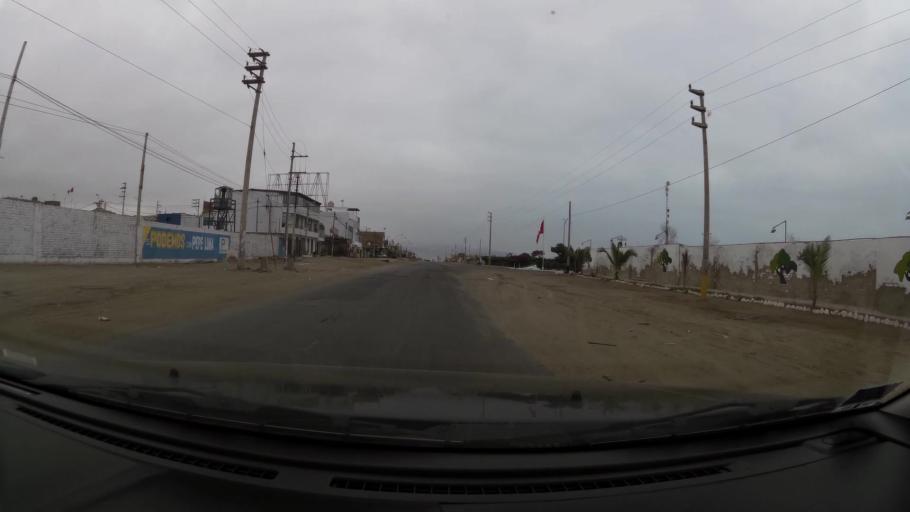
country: PE
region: Lima
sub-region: Lima
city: Punta Hermosa
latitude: -12.3471
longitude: -76.8138
